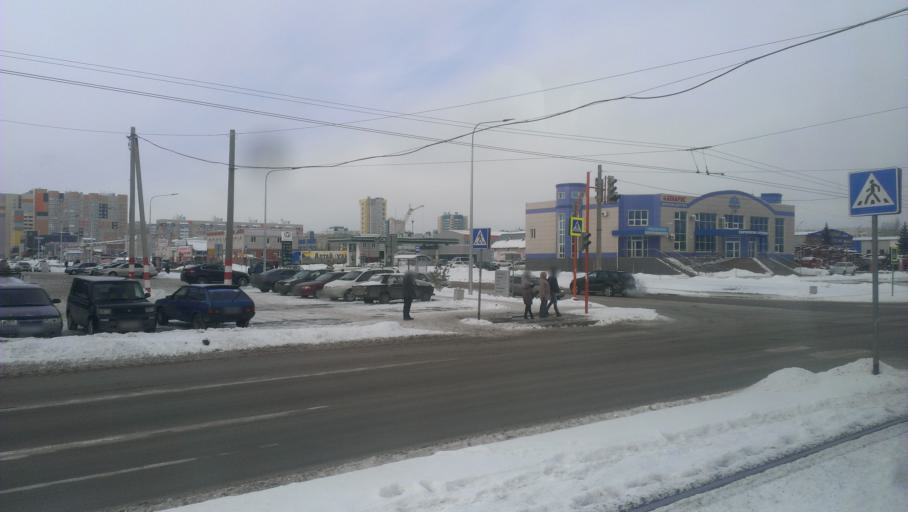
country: RU
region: Altai Krai
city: Novosilikatnyy
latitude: 53.3358
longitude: 83.6690
